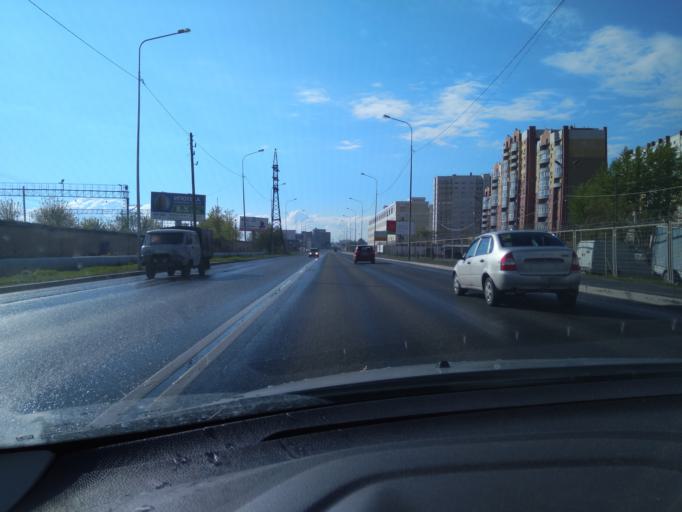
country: RU
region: Tjumen
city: Tyumen
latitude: 57.1373
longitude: 65.5491
